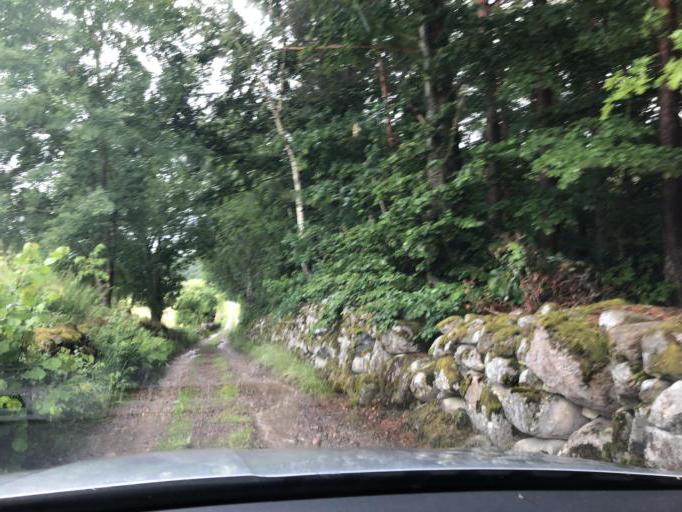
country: SE
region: Blekinge
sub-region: Solvesborgs Kommun
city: Soelvesborg
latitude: 56.1309
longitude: 14.6045
